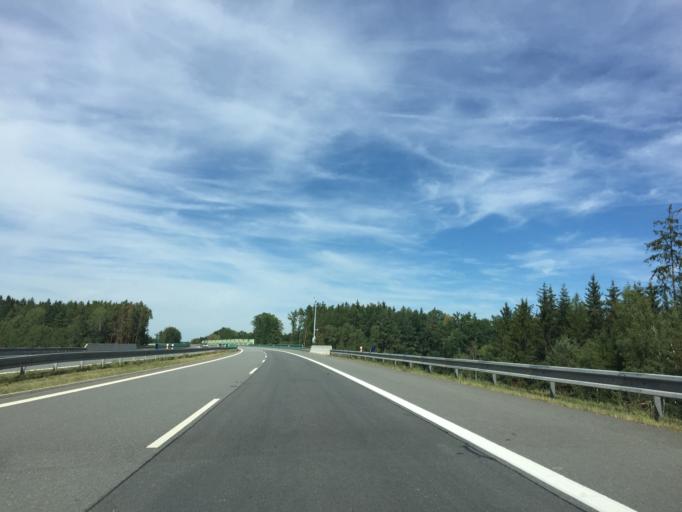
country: CZ
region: Jihocesky
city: Plana nad Luznici
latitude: 49.3799
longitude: 14.7246
